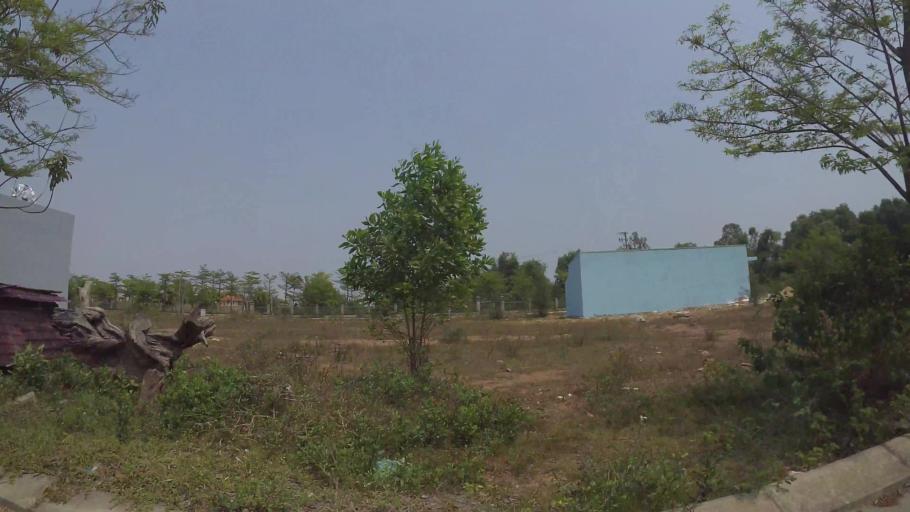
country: VN
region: Da Nang
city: Ngu Hanh Son
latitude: 15.9978
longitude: 108.2361
